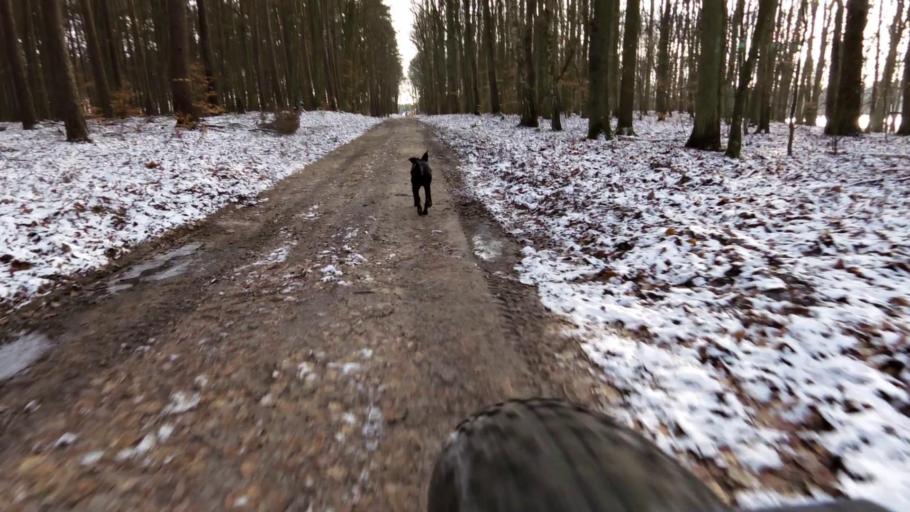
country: PL
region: West Pomeranian Voivodeship
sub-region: Powiat walecki
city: Walcz
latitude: 53.2745
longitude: 16.3076
